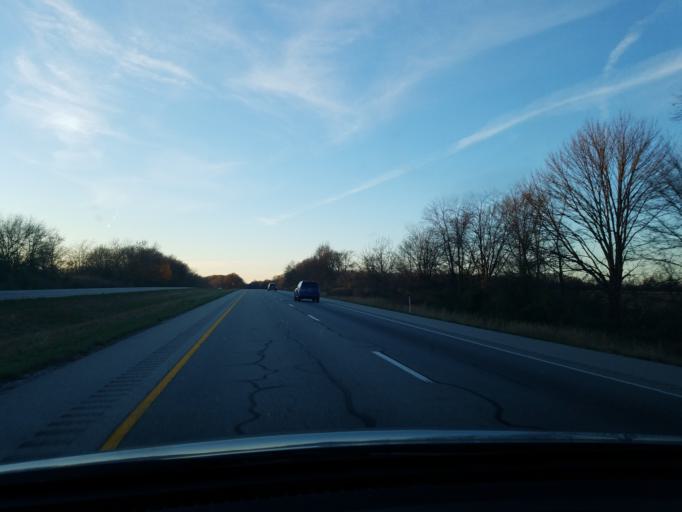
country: US
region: Indiana
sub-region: Posey County
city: Poseyville
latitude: 38.1898
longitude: -87.8323
